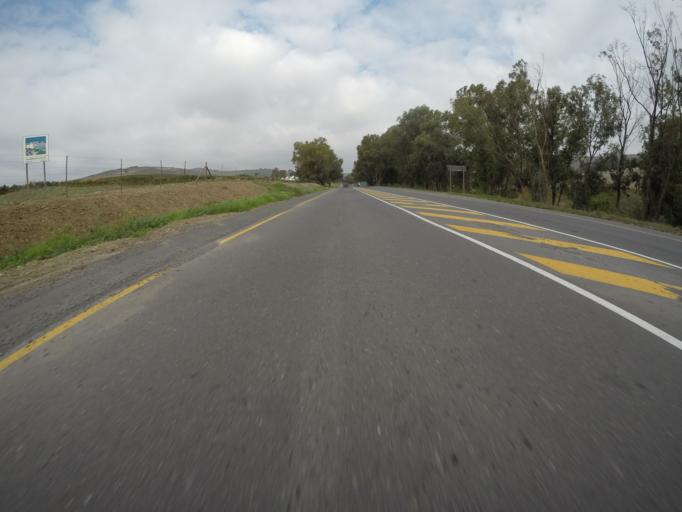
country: ZA
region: Western Cape
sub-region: City of Cape Town
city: Sunset Beach
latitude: -33.8213
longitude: 18.5758
